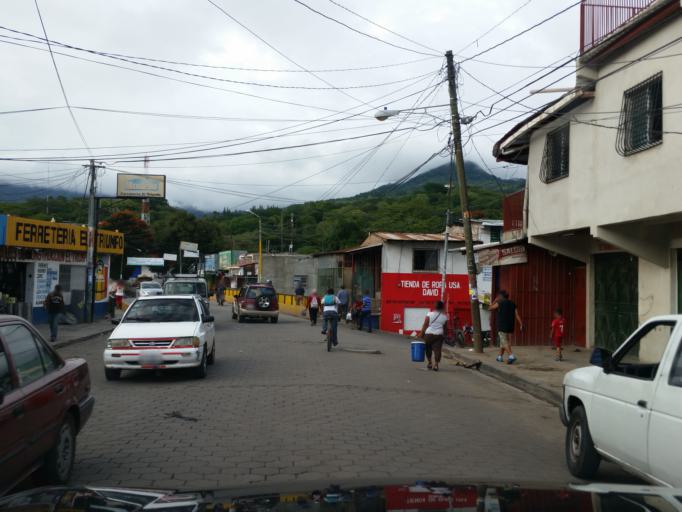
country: NI
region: Matagalpa
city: Matagalpa
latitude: 12.9356
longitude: -85.9115
